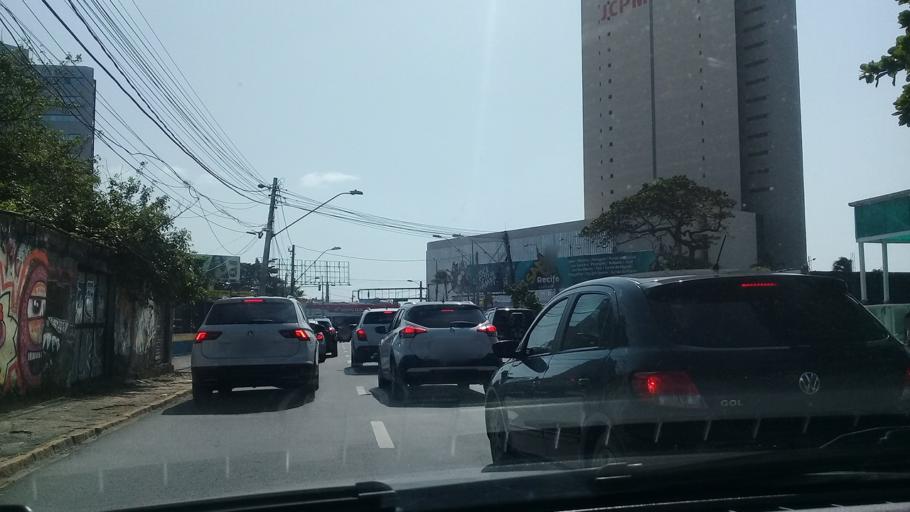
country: BR
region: Pernambuco
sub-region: Recife
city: Recife
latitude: -8.0904
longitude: -34.8836
